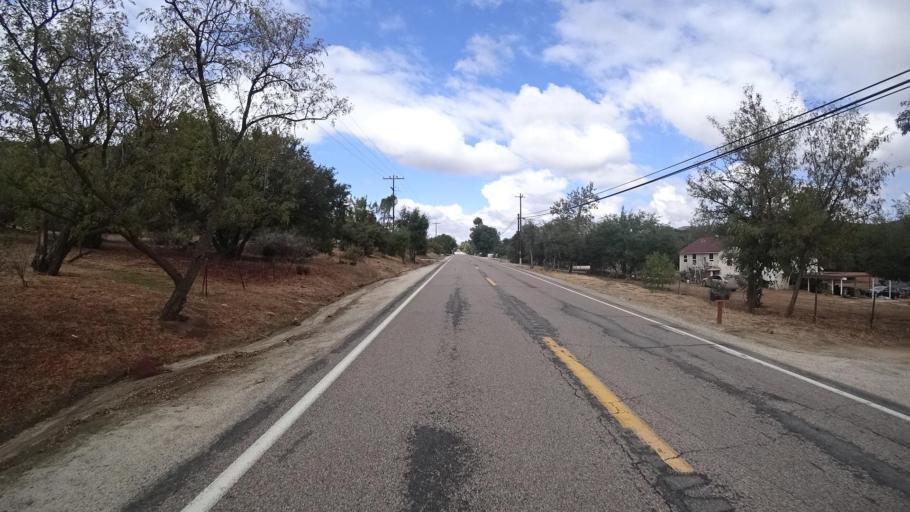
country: US
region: California
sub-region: San Diego County
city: Campo
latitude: 32.6575
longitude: -116.4878
